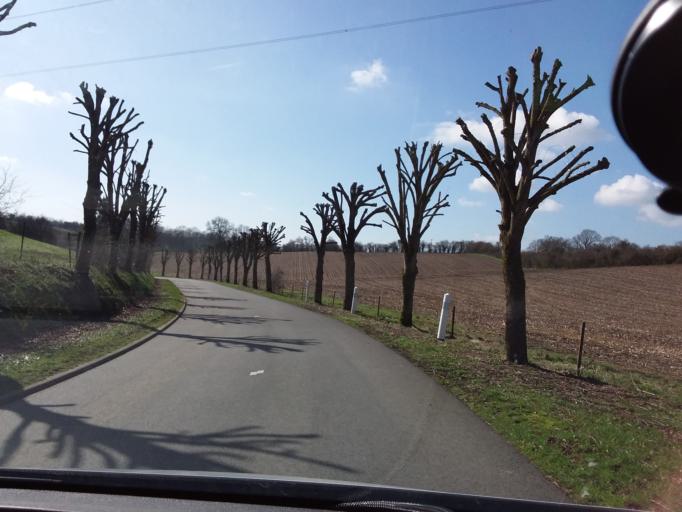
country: FR
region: Picardie
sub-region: Departement de l'Aisne
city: Hirson
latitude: 49.8838
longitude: 4.0956
